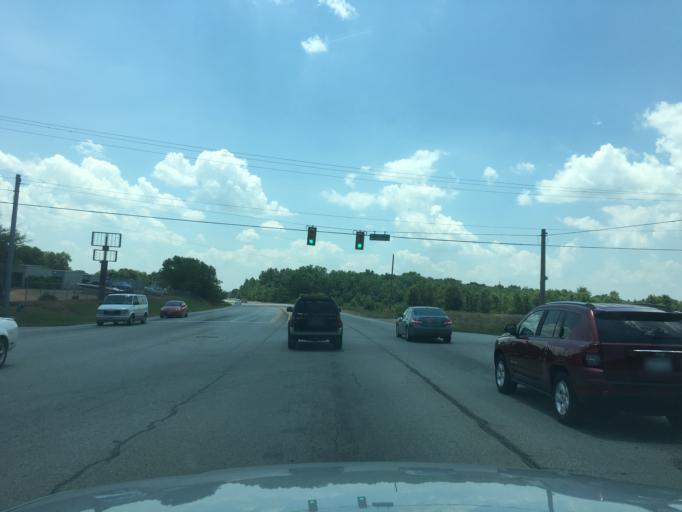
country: US
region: South Carolina
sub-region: Anderson County
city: Northlake
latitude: 34.6225
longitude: -82.6061
